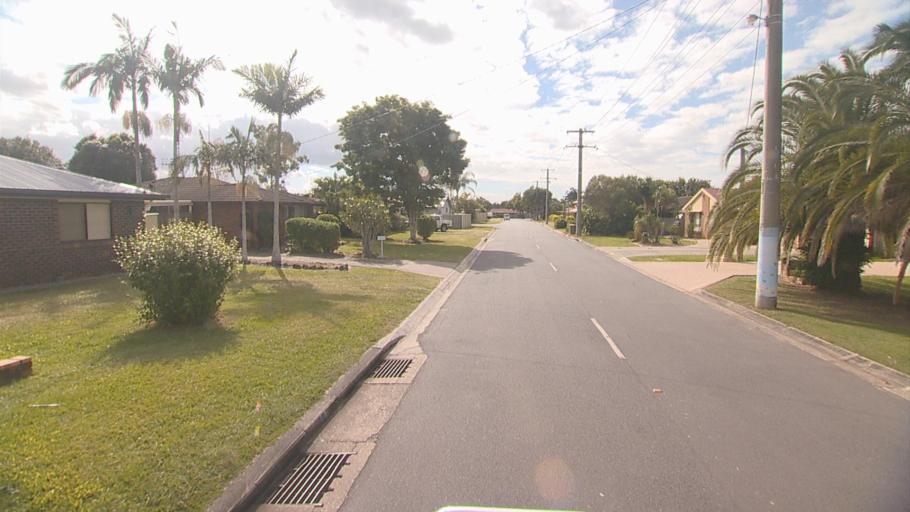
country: AU
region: Queensland
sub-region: Logan
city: Windaroo
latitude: -27.7372
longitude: 153.2099
